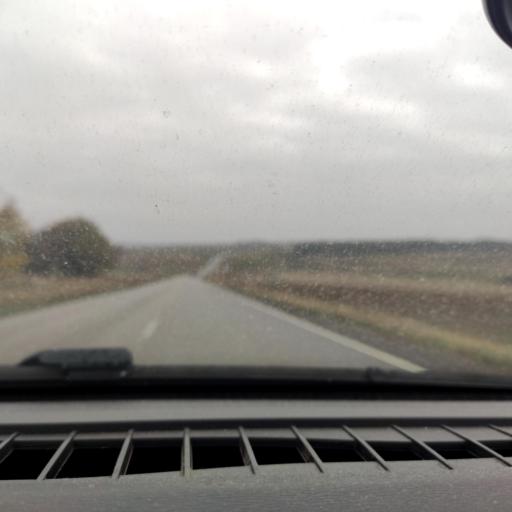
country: RU
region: Belgorod
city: Ilovka
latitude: 50.7657
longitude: 38.7485
